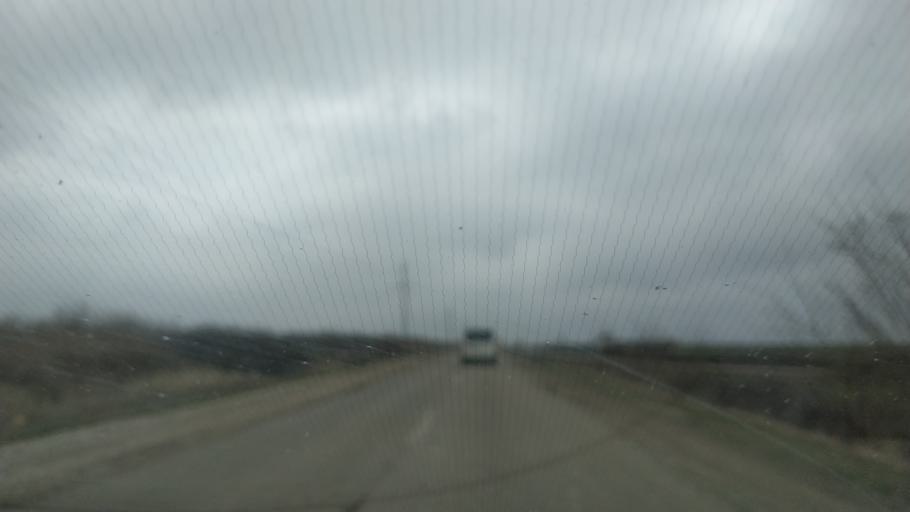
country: MD
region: Gagauzia
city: Bugeac
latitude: 46.3282
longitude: 28.7318
